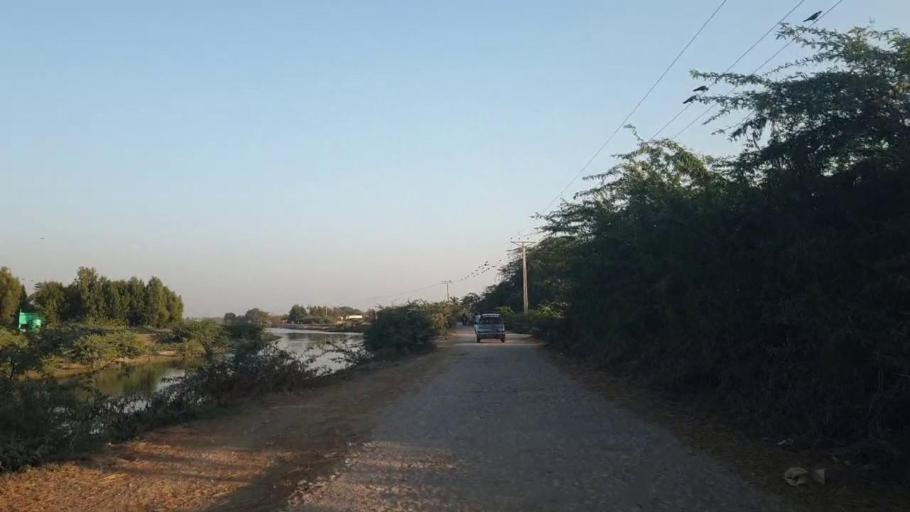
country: PK
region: Sindh
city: Mirpur Sakro
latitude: 24.4631
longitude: 67.5885
